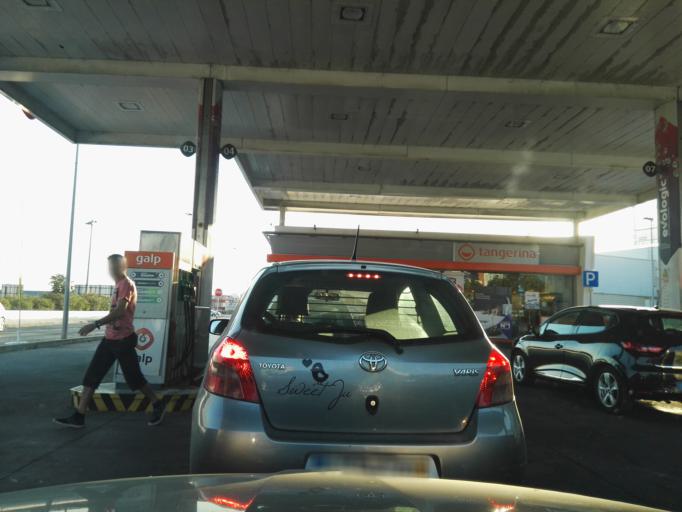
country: PT
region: Lisbon
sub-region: Vila Franca de Xira
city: Sobralinho
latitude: 38.8900
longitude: -9.0404
